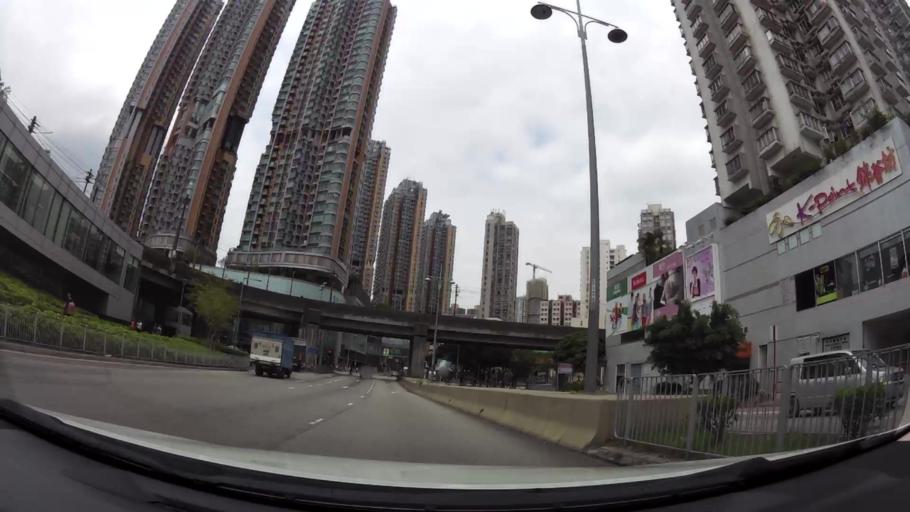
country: HK
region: Tuen Mun
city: Tuen Mun
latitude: 22.3935
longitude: 113.9750
